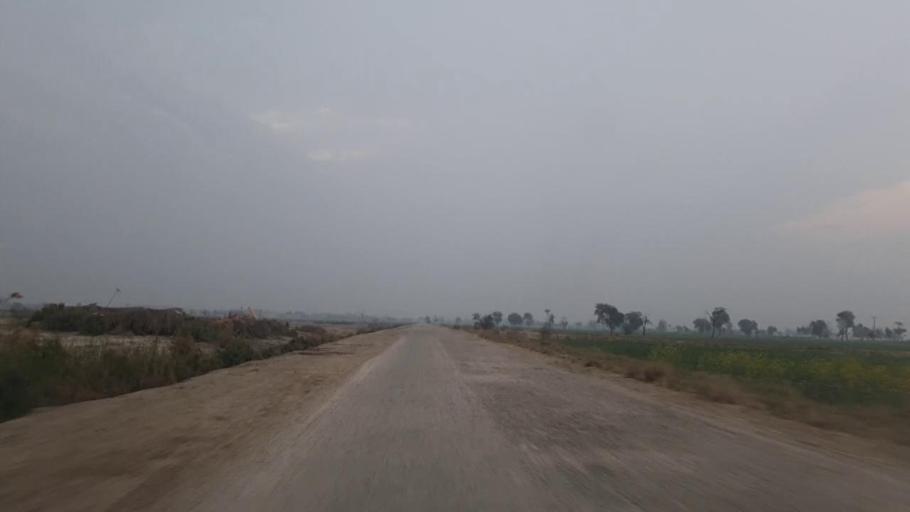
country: PK
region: Sindh
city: Jam Sahib
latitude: 26.3363
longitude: 68.5601
